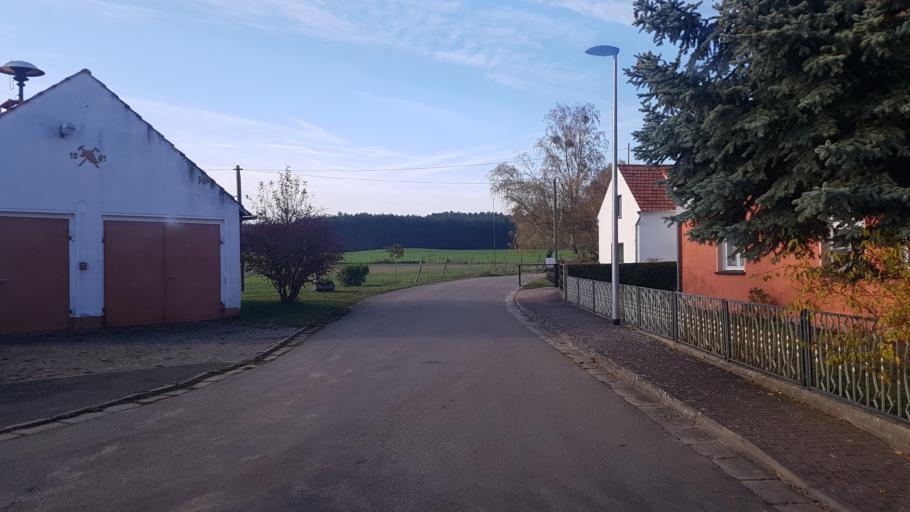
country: DE
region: Brandenburg
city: Calau
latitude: 51.6914
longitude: 13.9664
